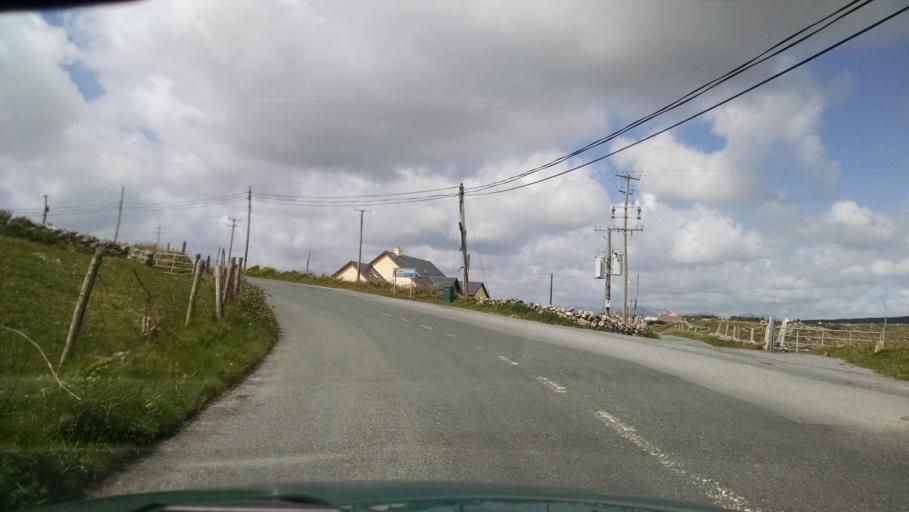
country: IE
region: Connaught
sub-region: County Galway
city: Clifden
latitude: 53.3079
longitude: -9.7822
